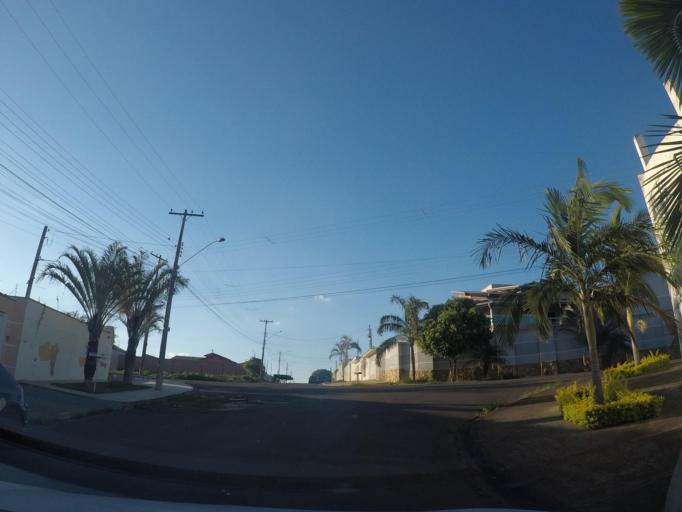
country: BR
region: Sao Paulo
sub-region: Sumare
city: Sumare
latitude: -22.8222
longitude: -47.2542
